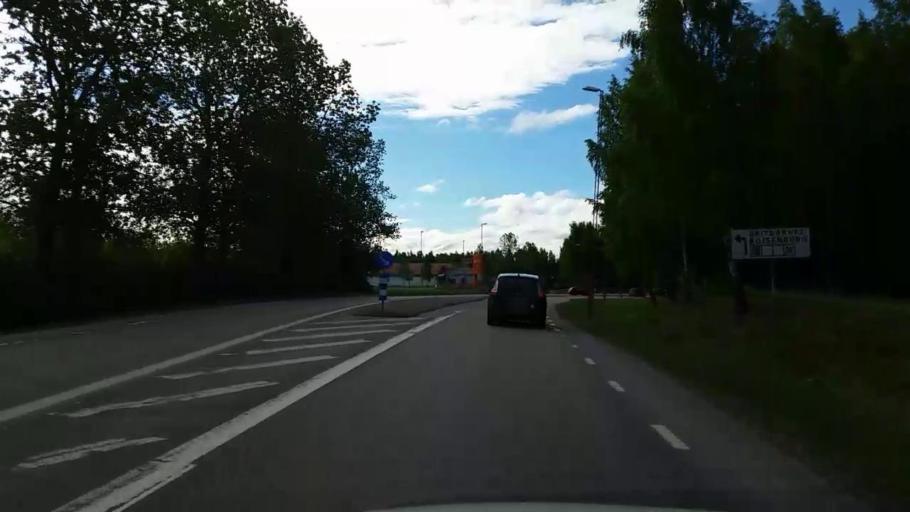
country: SE
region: Dalarna
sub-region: Faluns Kommun
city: Falun
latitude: 60.6241
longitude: 15.6147
